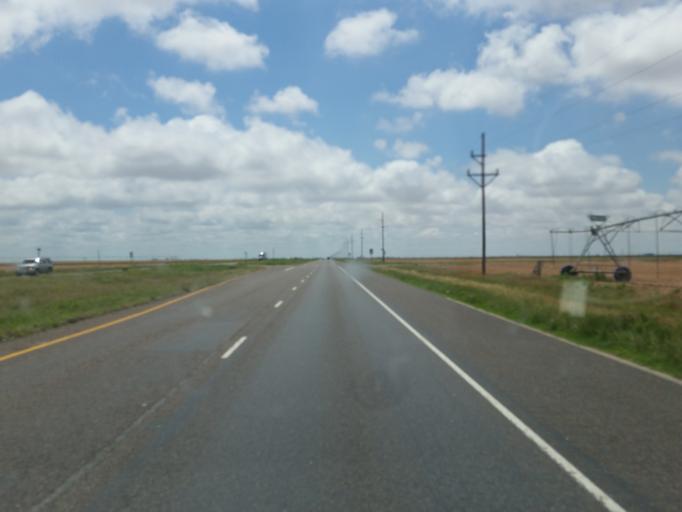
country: US
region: Texas
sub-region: Lubbock County
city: Slaton
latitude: 33.3928
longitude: -101.6026
